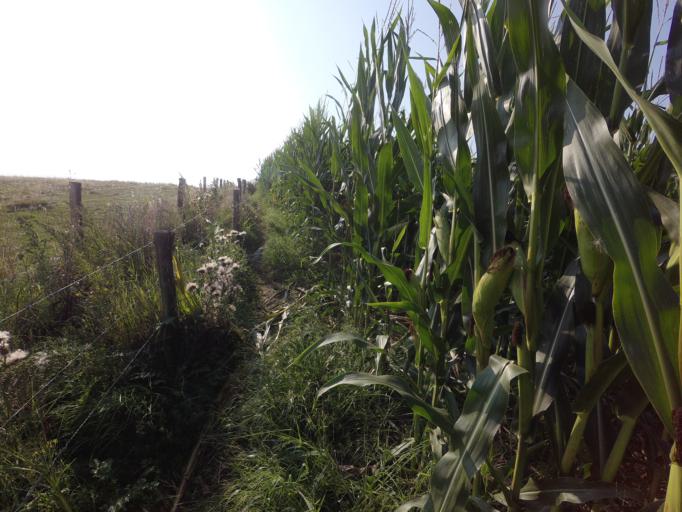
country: BE
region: Wallonia
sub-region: Province de Liege
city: Plombieres
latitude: 50.7789
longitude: 5.9038
